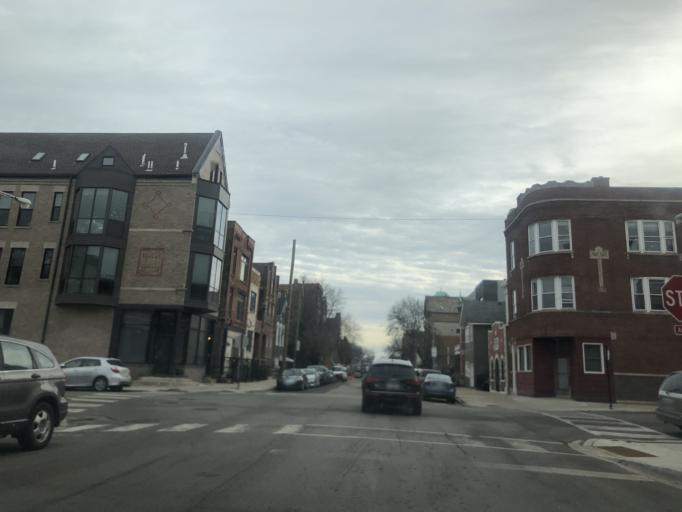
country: US
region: Illinois
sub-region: Cook County
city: Chicago
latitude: 41.9071
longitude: -87.6655
